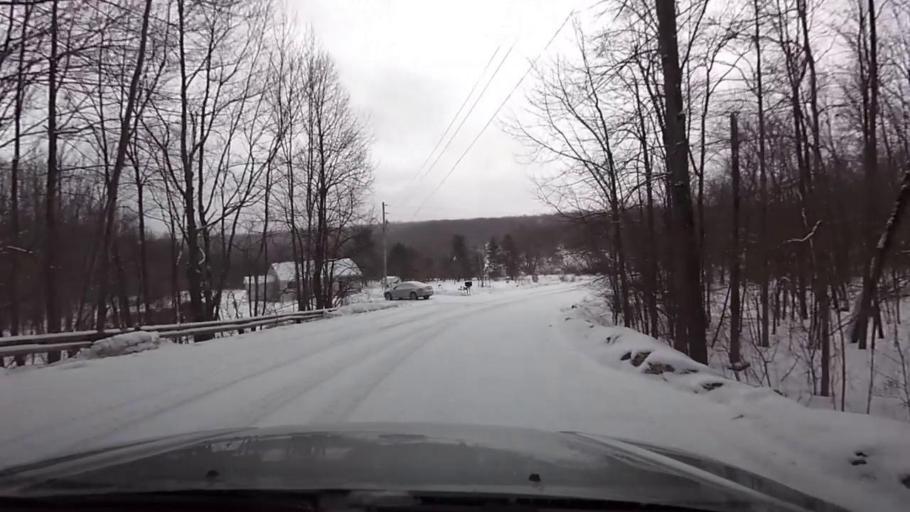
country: US
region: New York
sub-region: Cattaraugus County
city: Franklinville
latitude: 42.3379
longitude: -78.3545
